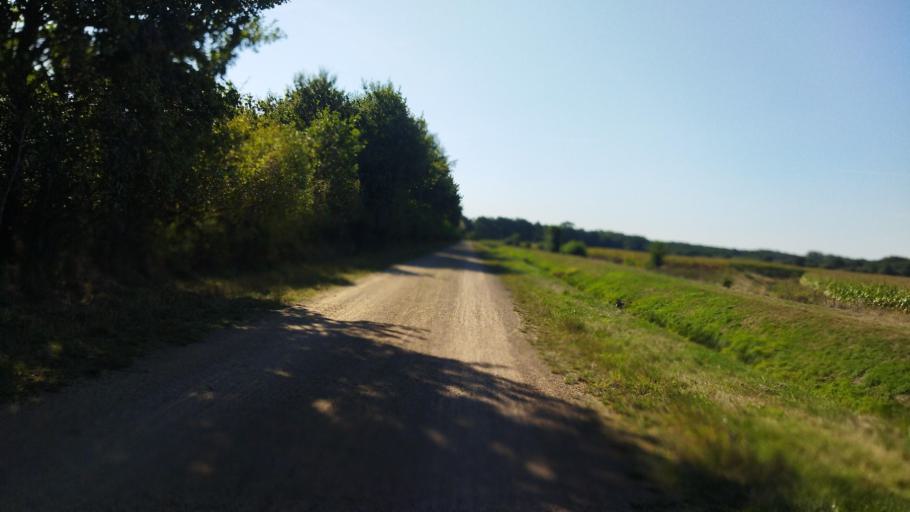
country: DE
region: Lower Saxony
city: Haren
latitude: 52.7749
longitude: 7.2708
